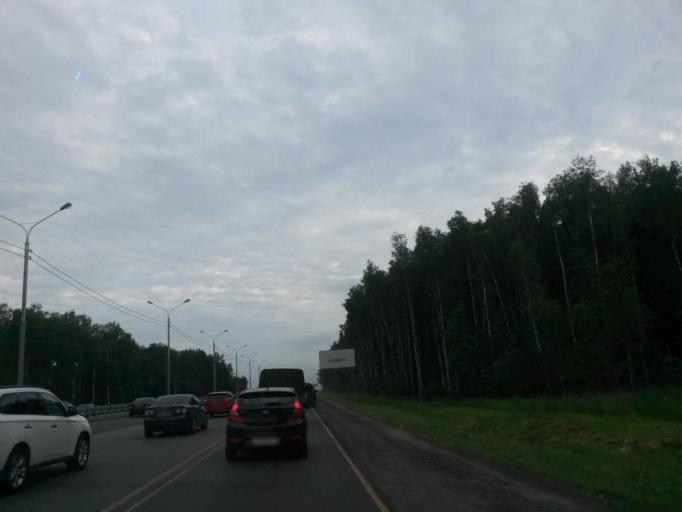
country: RU
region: Moskovskaya
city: Lyubuchany
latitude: 55.2634
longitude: 37.5345
